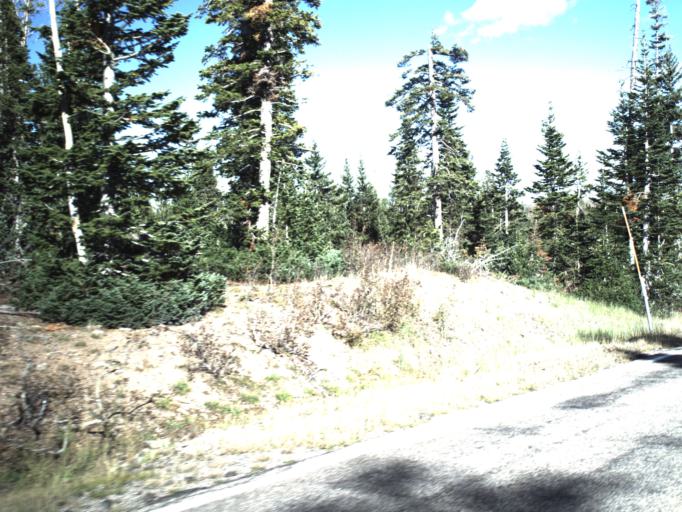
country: US
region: Utah
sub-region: Iron County
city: Parowan
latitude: 37.6532
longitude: -112.8039
